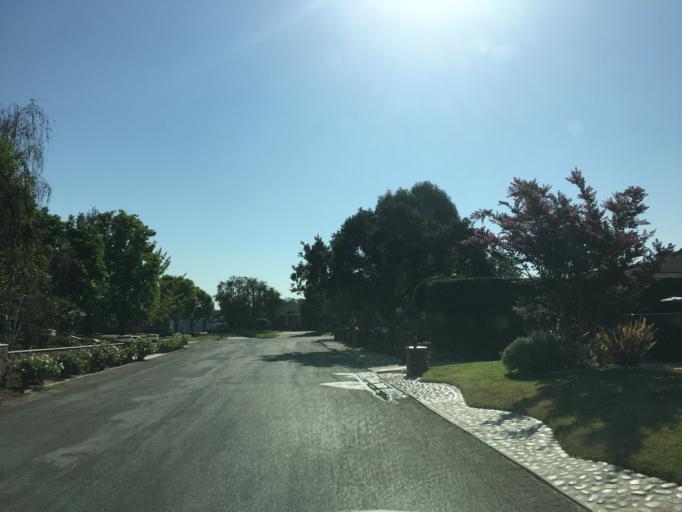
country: US
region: California
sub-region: Los Angeles County
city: Charter Oak
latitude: 34.0868
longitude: -117.8398
